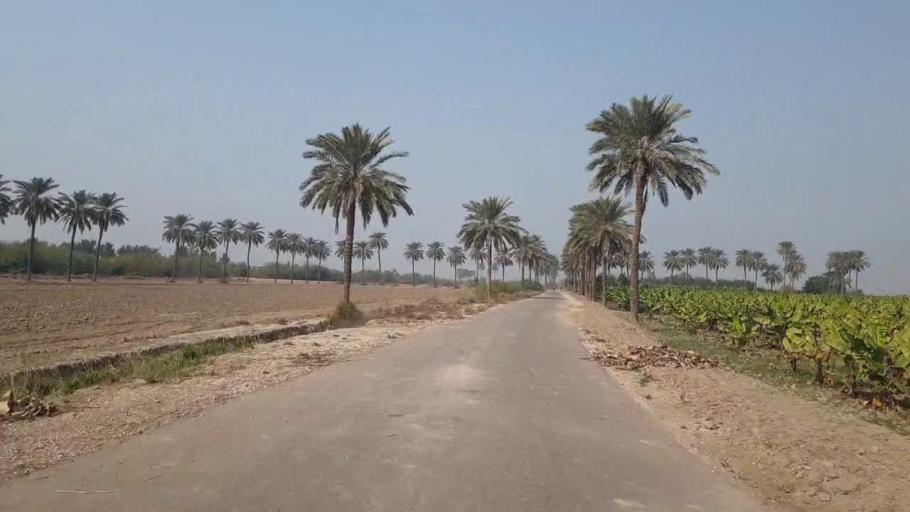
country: PK
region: Sindh
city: Bhit Shah
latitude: 25.7772
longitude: 68.4786
